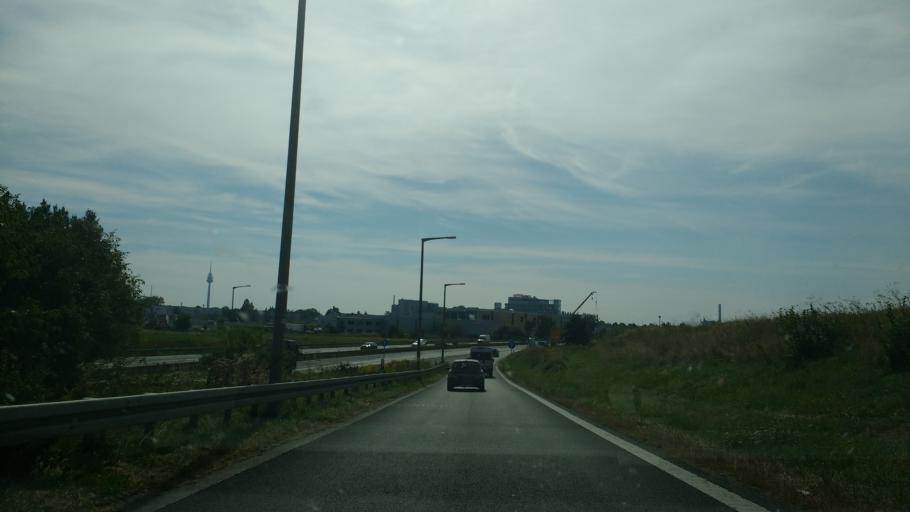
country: DE
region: Bavaria
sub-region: Regierungsbezirk Mittelfranken
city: Grossreuth bei Schweinau
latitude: 49.4469
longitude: 10.9987
